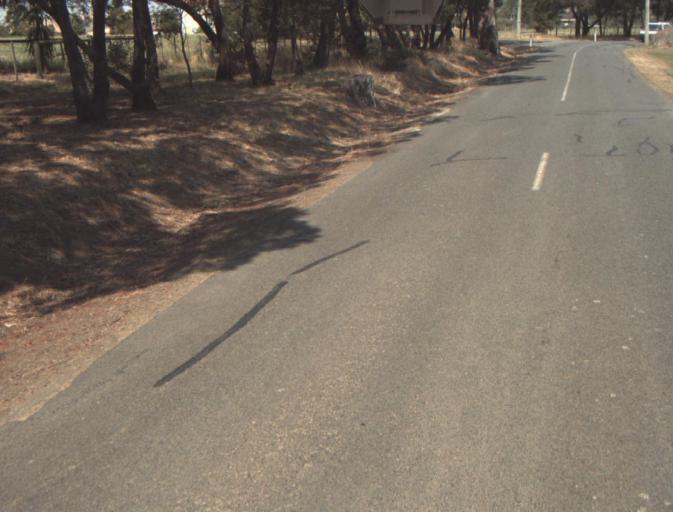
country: AU
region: Tasmania
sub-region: Northern Midlands
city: Perth
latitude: -41.5026
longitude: 147.2056
